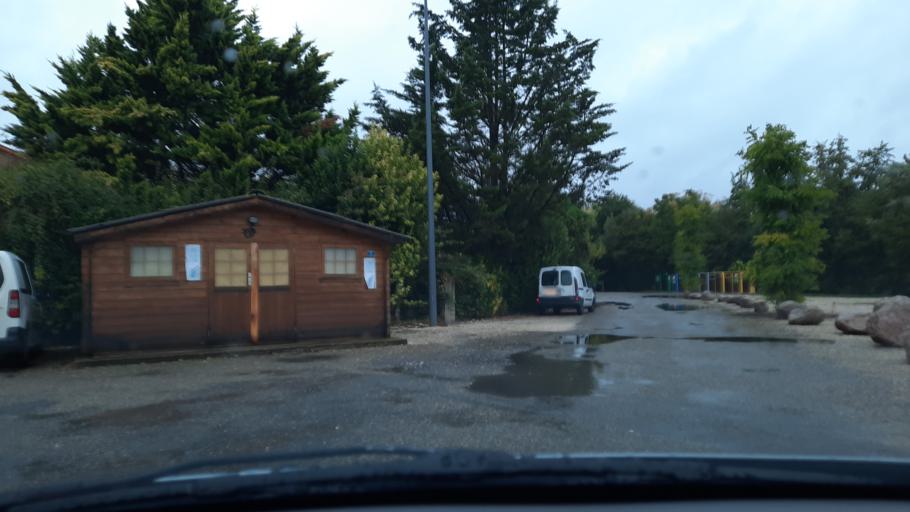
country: FR
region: Midi-Pyrenees
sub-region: Departement du Tarn-et-Garonne
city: Lafrancaise
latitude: 44.1891
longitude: 1.2859
